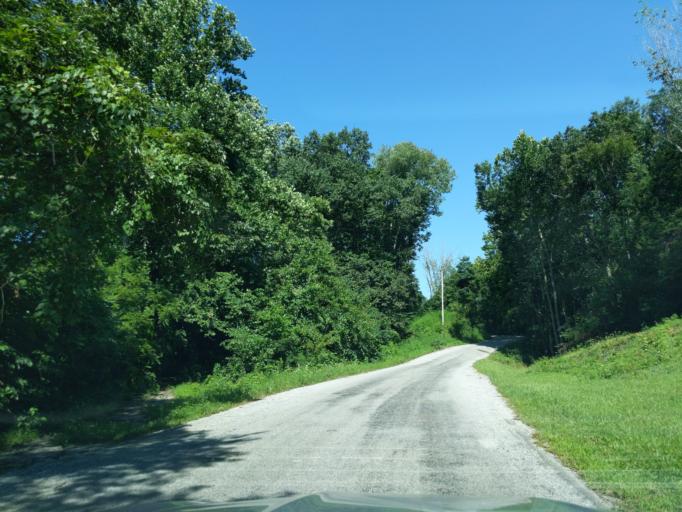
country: US
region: Indiana
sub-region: Ripley County
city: Osgood
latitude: 39.0759
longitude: -85.4265
